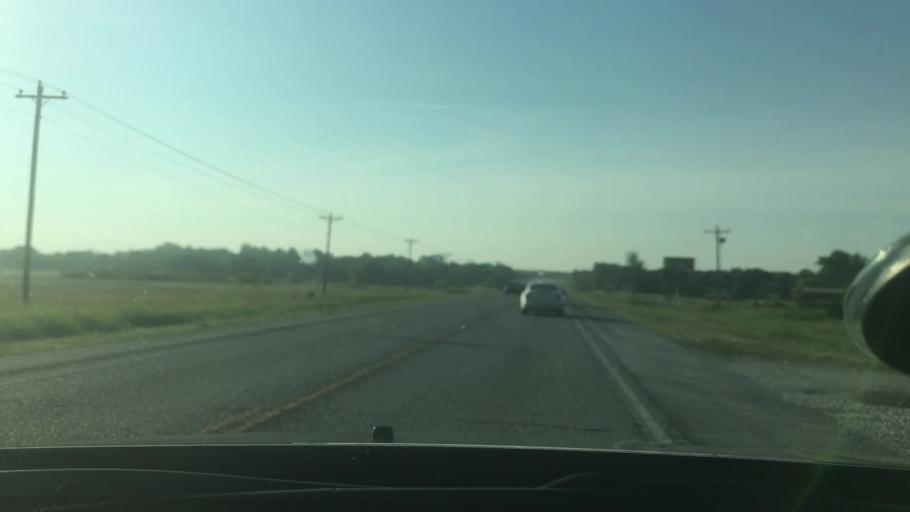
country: US
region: Oklahoma
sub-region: Pontotoc County
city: Ada
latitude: 34.8065
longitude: -96.7493
